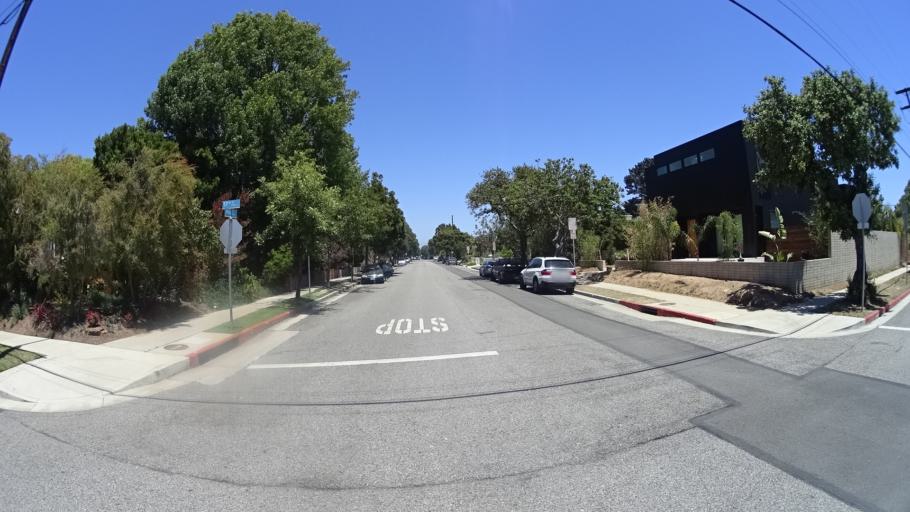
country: US
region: California
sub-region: Los Angeles County
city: Santa Monica
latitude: 34.0110
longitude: -118.4653
